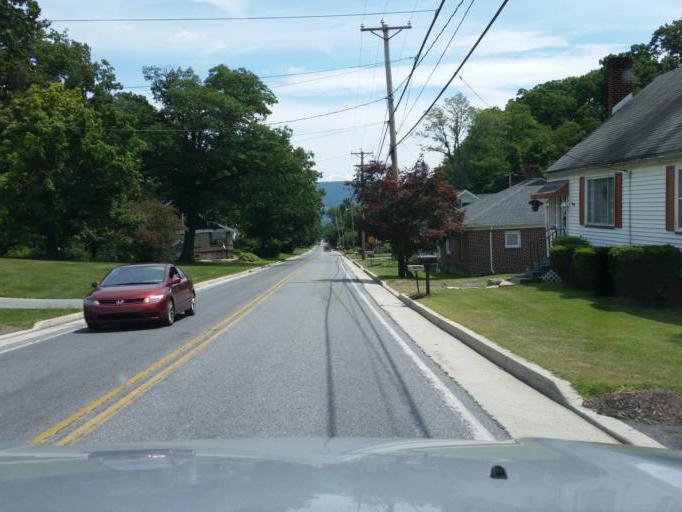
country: US
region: Pennsylvania
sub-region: Blair County
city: Altoona
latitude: 40.5513
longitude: -78.4362
